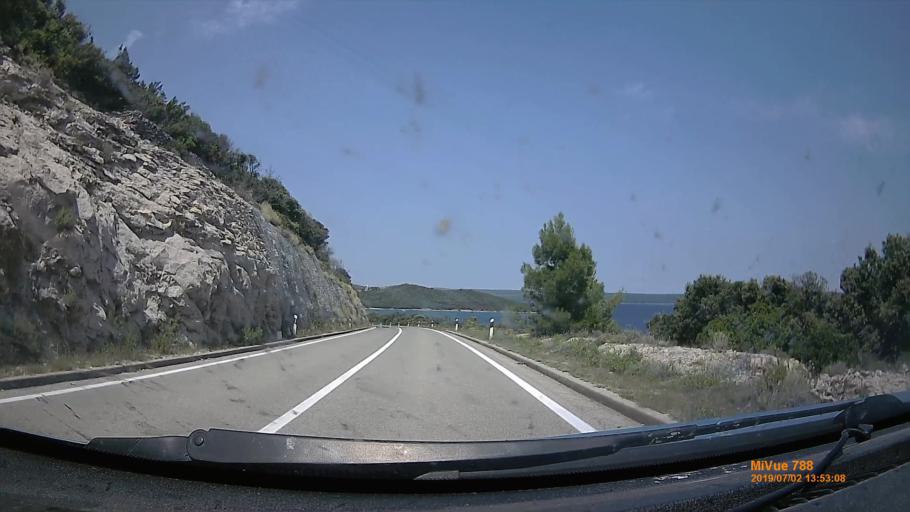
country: HR
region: Primorsko-Goranska
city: Mali Losinj
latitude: 44.6223
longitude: 14.3936
